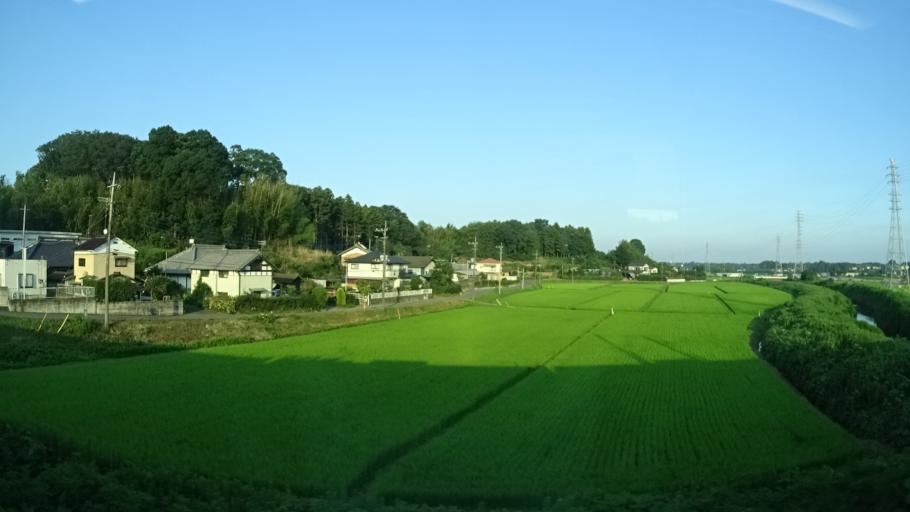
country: JP
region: Ibaraki
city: Ishioka
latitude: 36.2211
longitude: 140.2852
